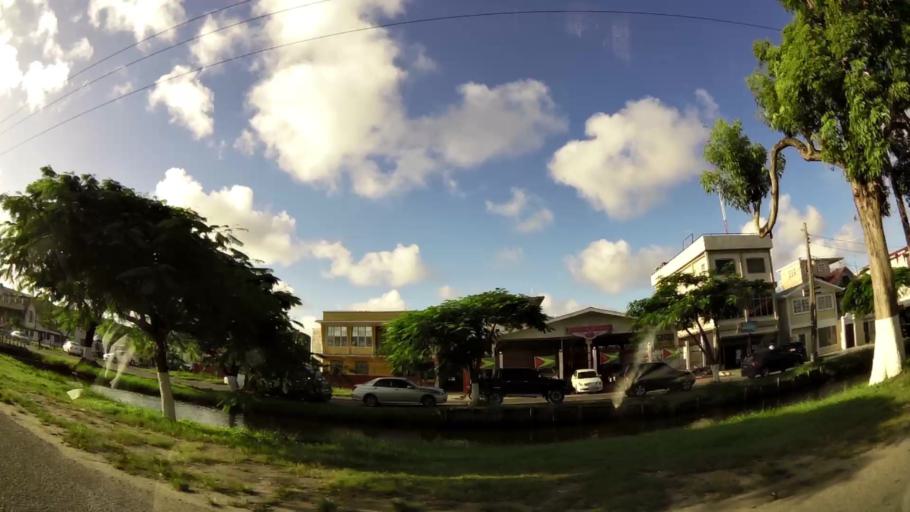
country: GY
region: Demerara-Mahaica
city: Georgetown
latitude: 6.8076
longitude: -58.1578
